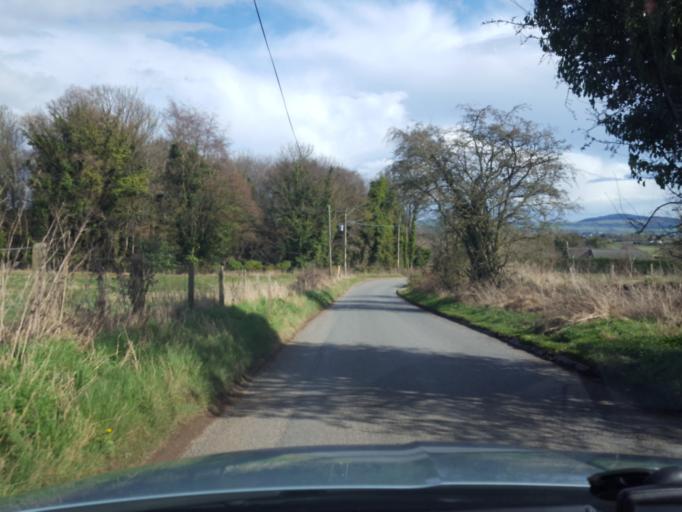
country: GB
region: Scotland
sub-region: Perth and Kinross
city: Errol
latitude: 56.4259
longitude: -3.2519
